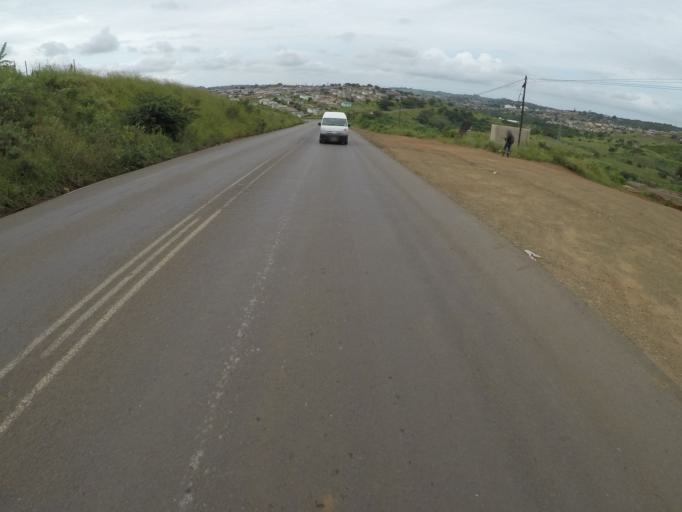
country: ZA
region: KwaZulu-Natal
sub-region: uThungulu District Municipality
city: Empangeni
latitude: -28.7637
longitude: 31.8755
